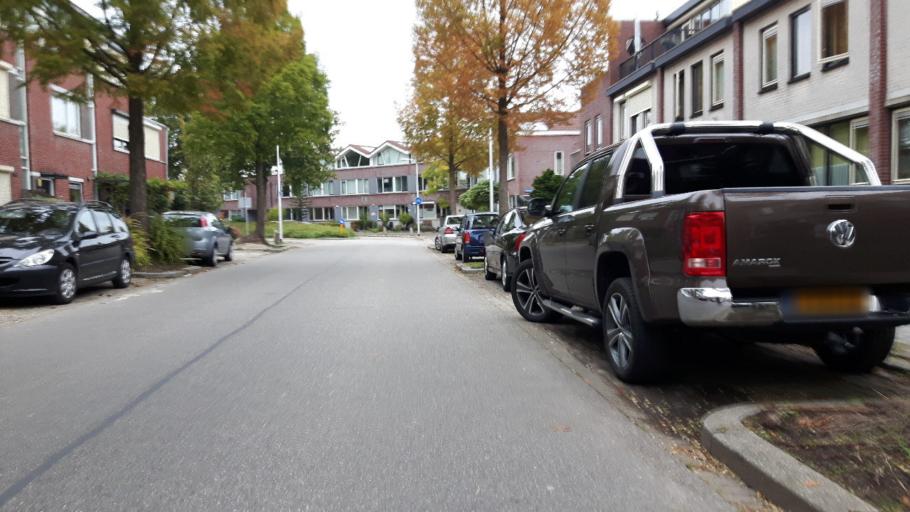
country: NL
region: South Holland
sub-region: Gemeente Vlist
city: Haastrecht
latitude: 52.0122
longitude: 4.7493
